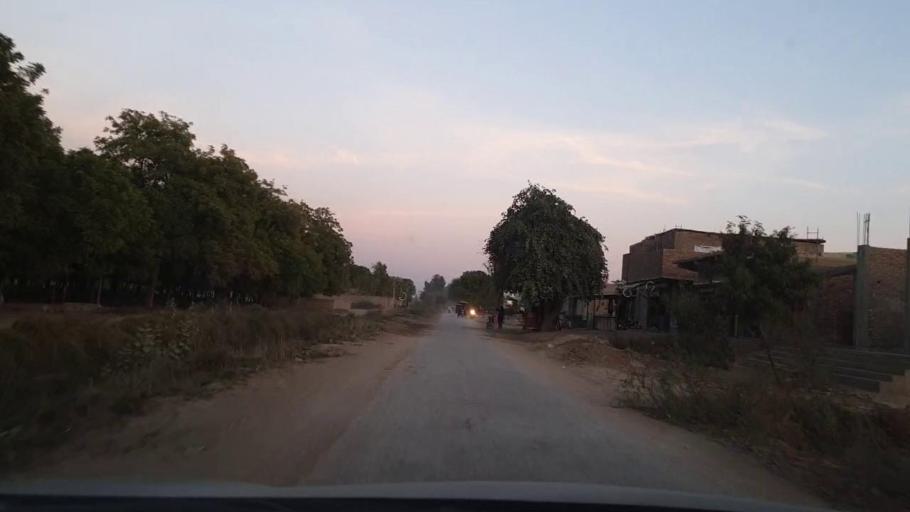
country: PK
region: Sindh
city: Tando Allahyar
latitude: 25.5532
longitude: 68.7951
